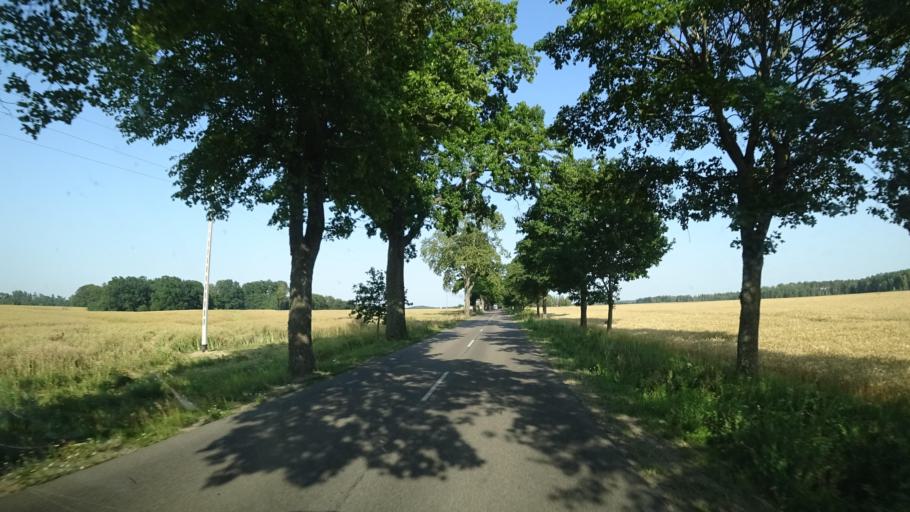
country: PL
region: Pomeranian Voivodeship
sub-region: Powiat czluchowski
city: Przechlewo
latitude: 53.8041
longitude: 17.2981
